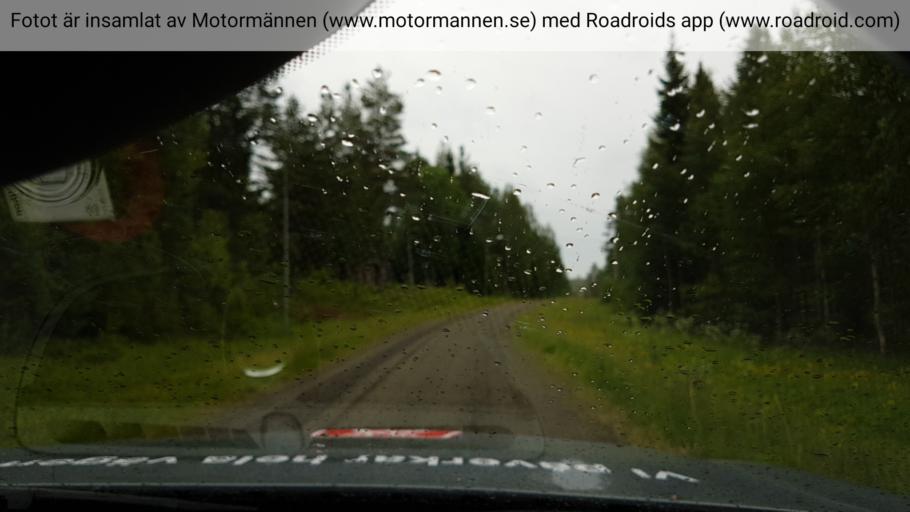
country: SE
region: Jaemtland
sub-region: Bergs Kommun
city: Hoverberg
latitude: 62.5688
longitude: 14.6699
